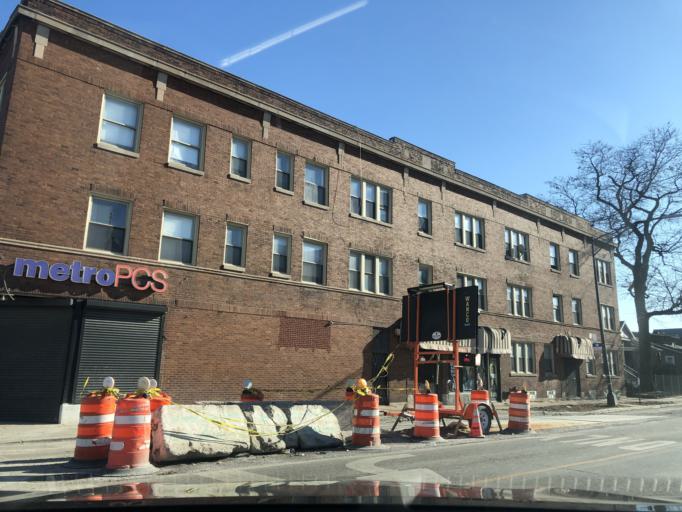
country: US
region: Indiana
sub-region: Lake County
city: Whiting
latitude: 41.7588
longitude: -87.5762
